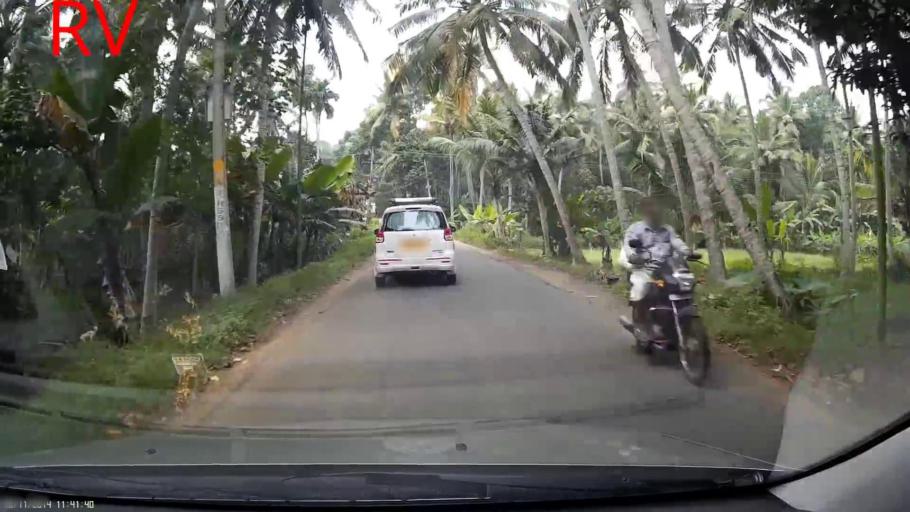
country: IN
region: Kerala
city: Kovalam
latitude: 8.4009
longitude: 77.0167
